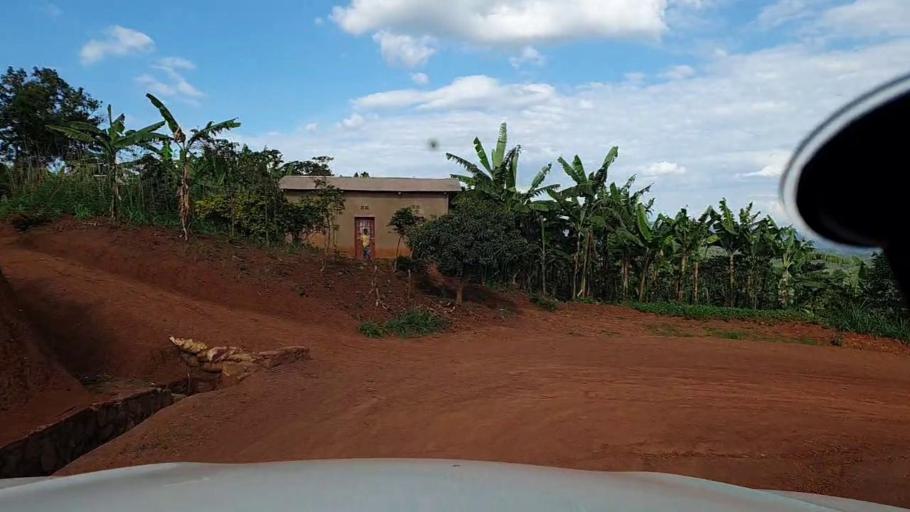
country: RW
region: Kigali
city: Kigali
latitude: -1.8379
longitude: 29.8522
